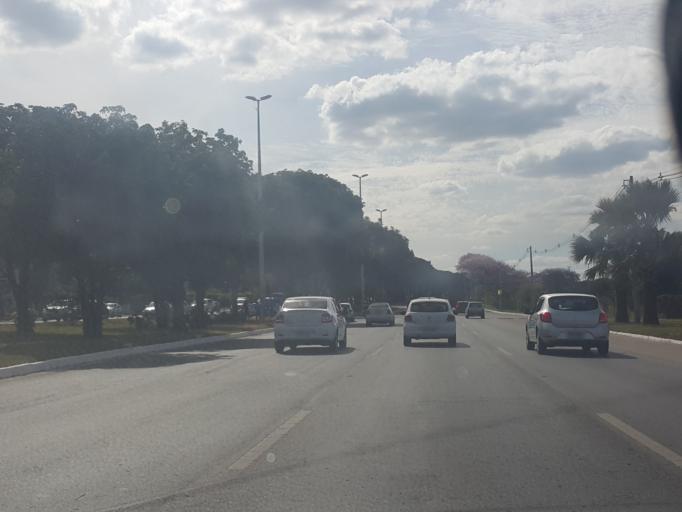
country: BR
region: Federal District
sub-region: Brasilia
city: Brasilia
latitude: -15.8257
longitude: -48.0545
